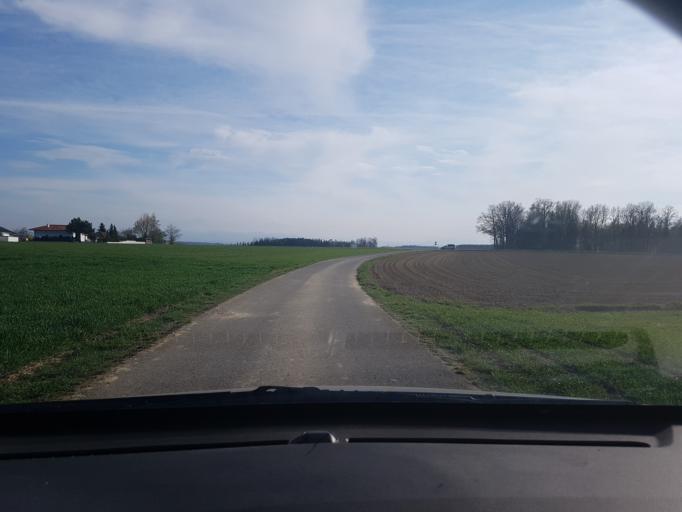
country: AT
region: Upper Austria
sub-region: Politischer Bezirk Linz-Land
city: Ansfelden
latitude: 48.1648
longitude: 14.3258
